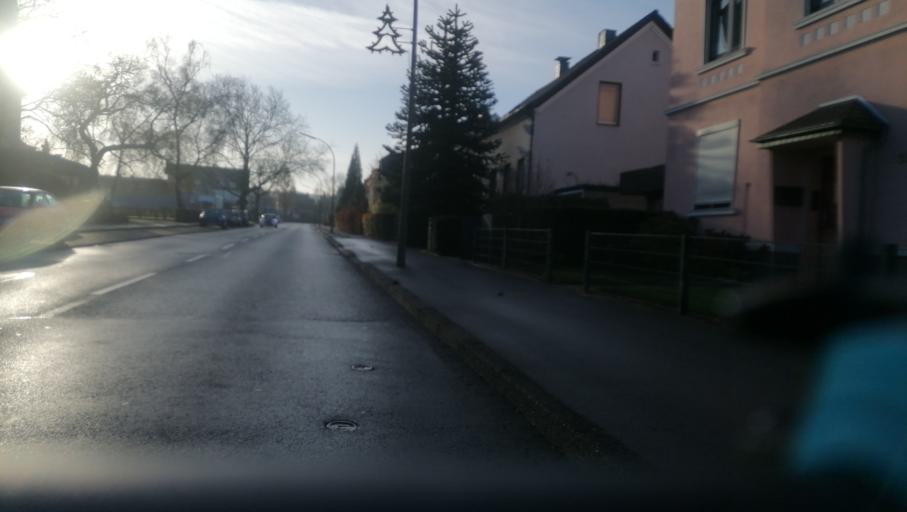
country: DE
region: North Rhine-Westphalia
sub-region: Regierungsbezirk Arnsberg
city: Dortmund
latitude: 51.4667
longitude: 7.4934
